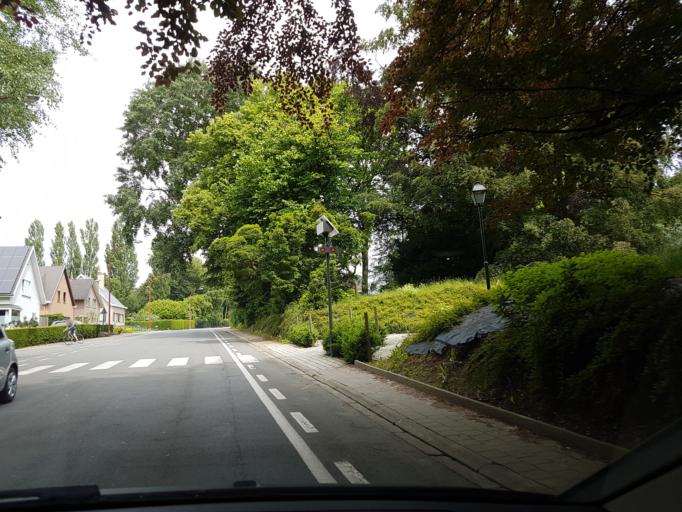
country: BE
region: Flanders
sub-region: Provincie Vlaams-Brabant
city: Asse
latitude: 50.9051
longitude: 4.2040
